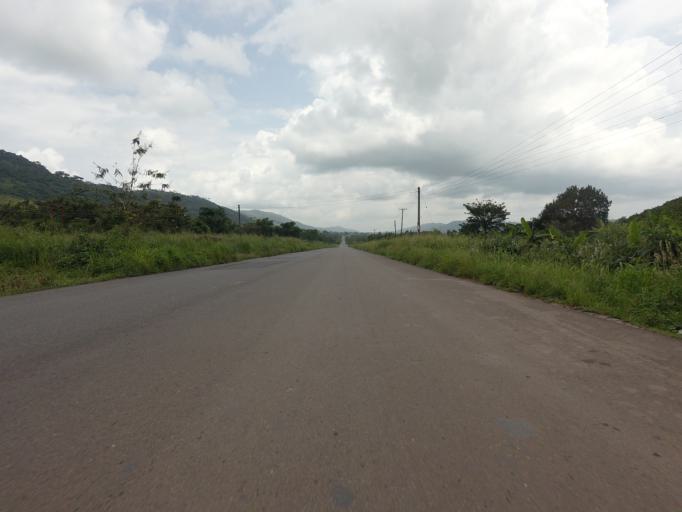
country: GH
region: Volta
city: Ho
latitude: 6.6200
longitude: 0.3066
